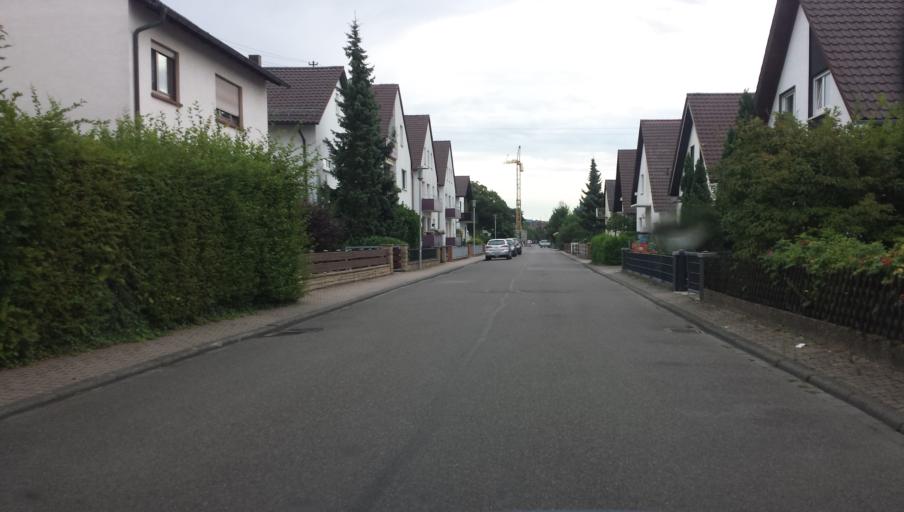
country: DE
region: Baden-Wuerttemberg
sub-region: Karlsruhe Region
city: Walldorf
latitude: 49.3098
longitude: 8.6361
